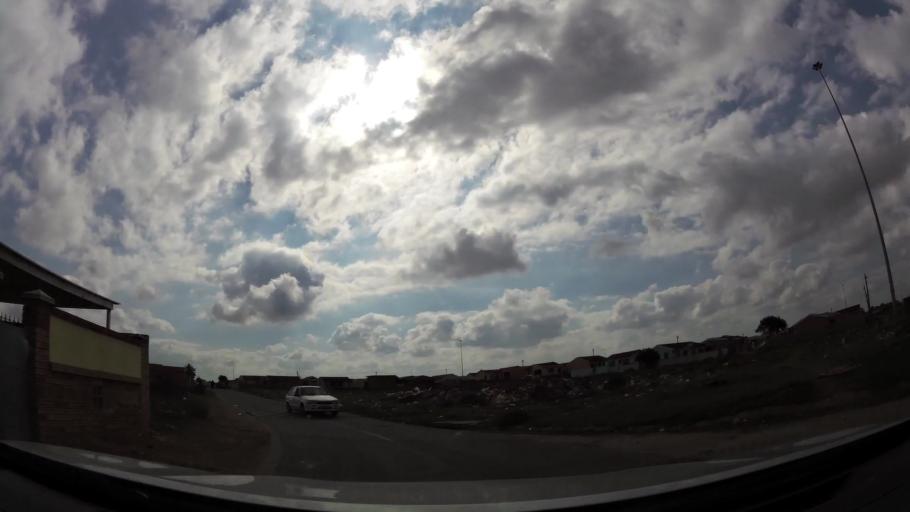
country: ZA
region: Eastern Cape
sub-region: Nelson Mandela Bay Metropolitan Municipality
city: Port Elizabeth
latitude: -33.8110
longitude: 25.5896
